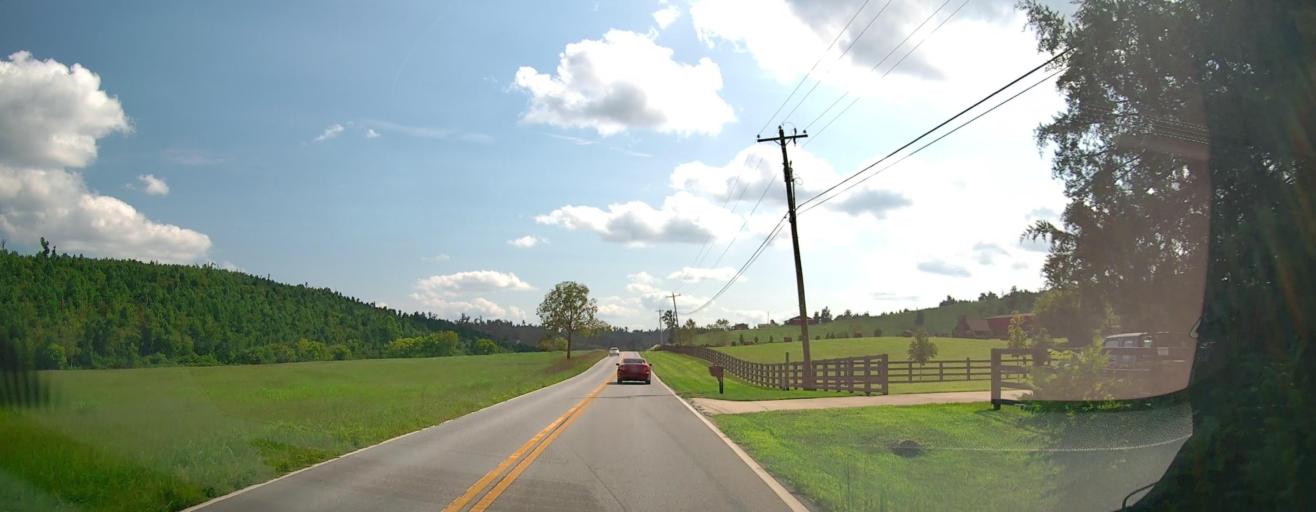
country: US
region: Tennessee
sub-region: Hamilton County
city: Apison
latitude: 34.9721
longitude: -85.0674
